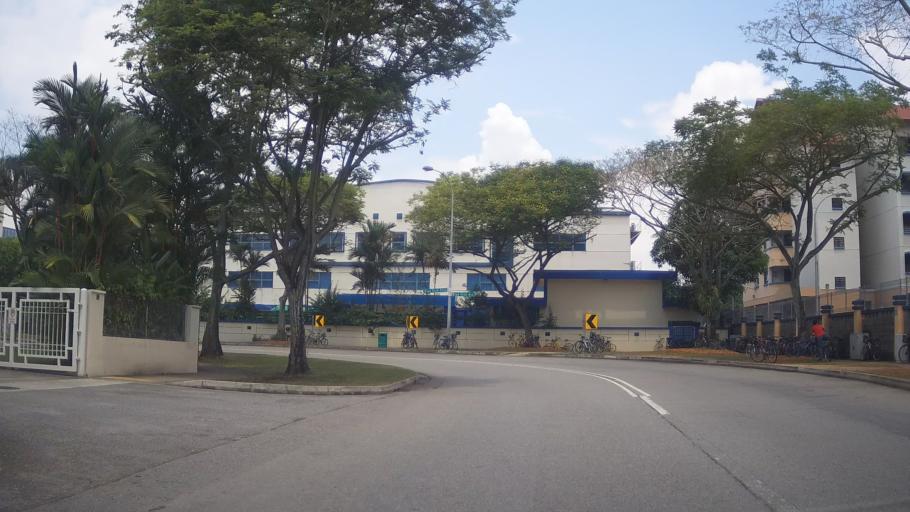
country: MY
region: Johor
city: Johor Bahru
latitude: 1.3331
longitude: 103.6934
